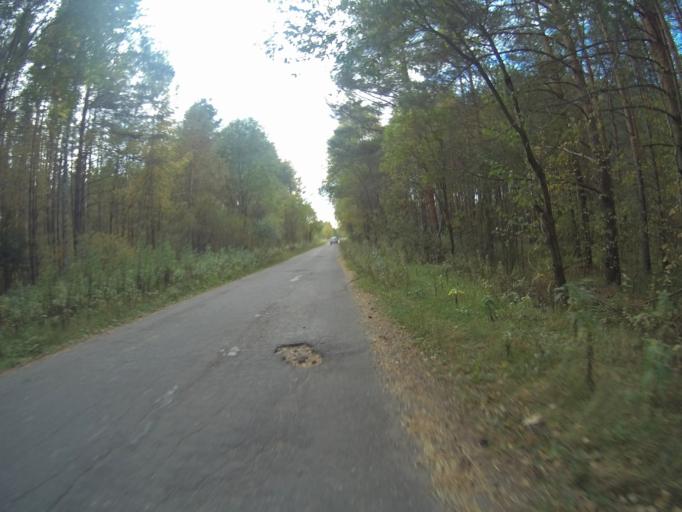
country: RU
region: Vladimir
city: Golovino
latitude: 55.9658
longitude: 40.4165
